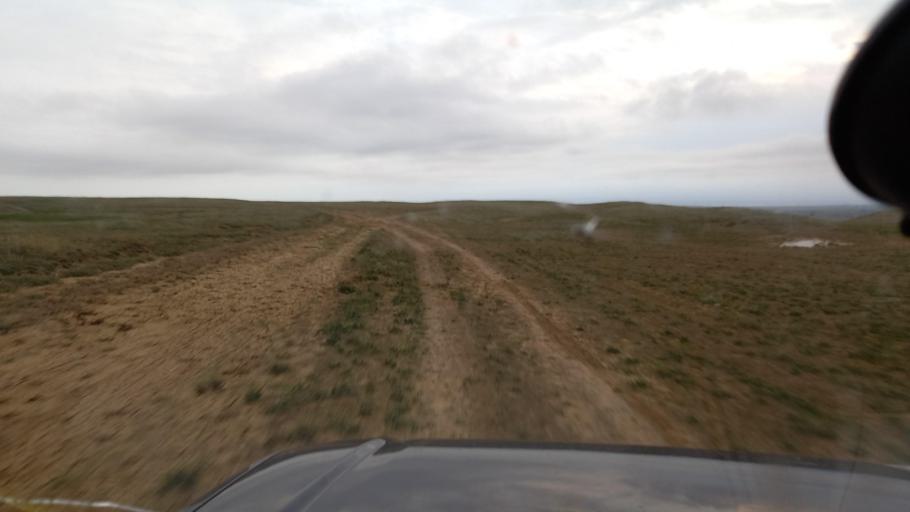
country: RU
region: Krasnodarskiy
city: Taman'
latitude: 45.2064
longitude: 36.7835
